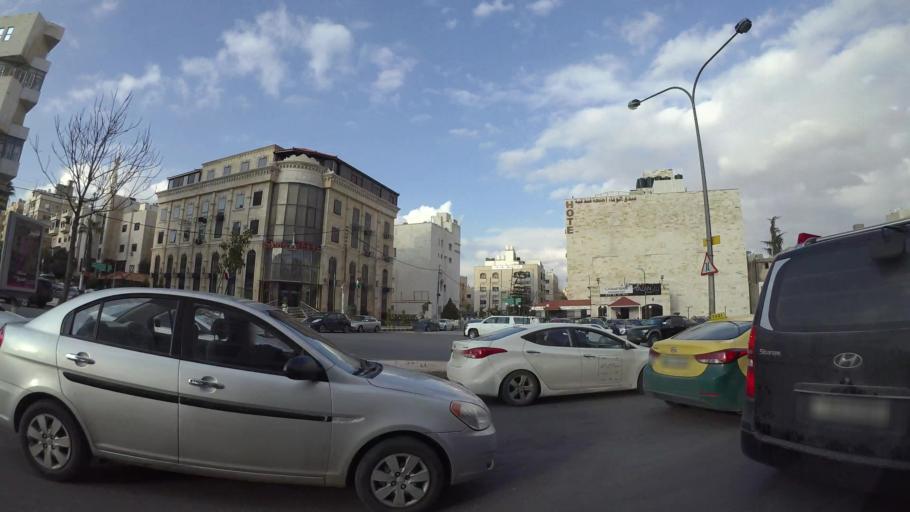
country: JO
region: Amman
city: Al Jubayhah
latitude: 31.9832
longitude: 35.8919
